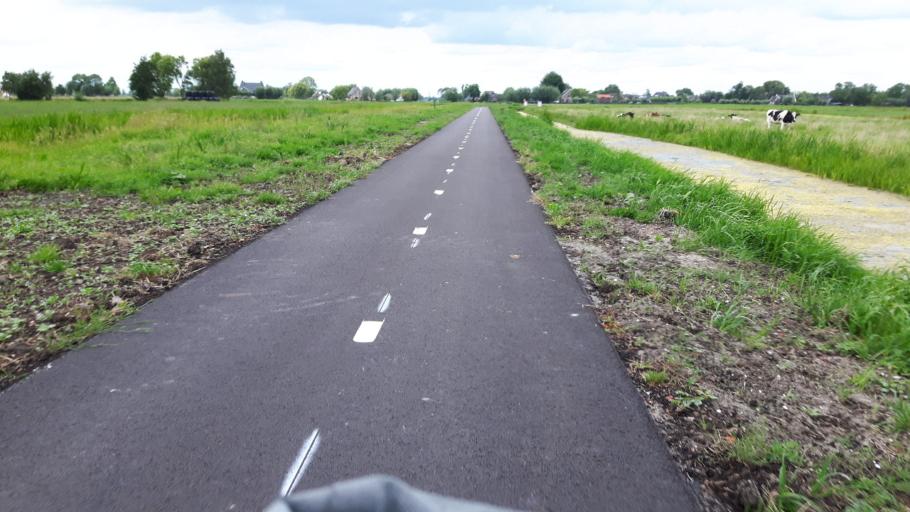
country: NL
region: South Holland
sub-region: Gemeente Vlist
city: Haastrecht
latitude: 51.9576
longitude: 4.7437
